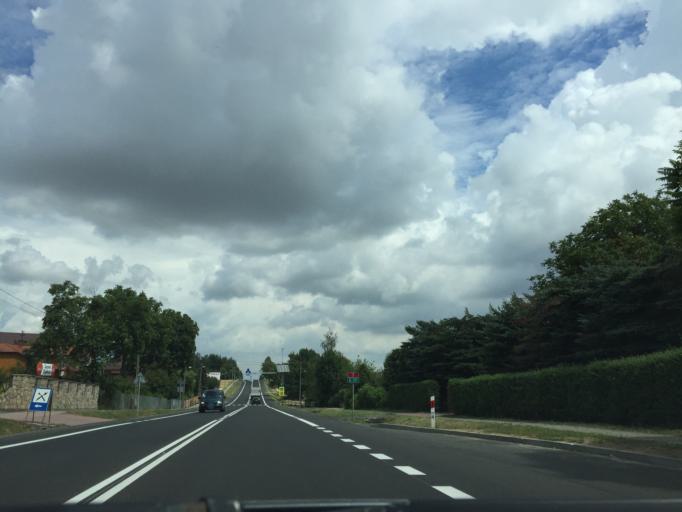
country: PL
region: Lesser Poland Voivodeship
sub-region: Powiat krakowski
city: Michalowice
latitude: 50.2041
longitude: 20.0134
